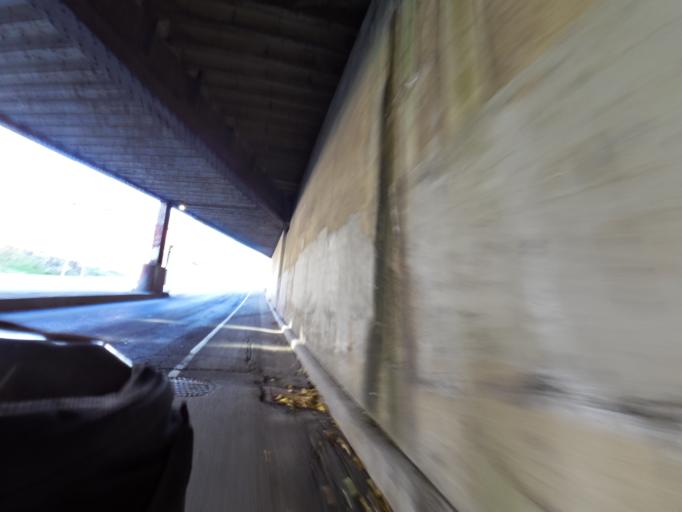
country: CA
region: Ontario
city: Hamilton
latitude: 43.2491
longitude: -79.8627
